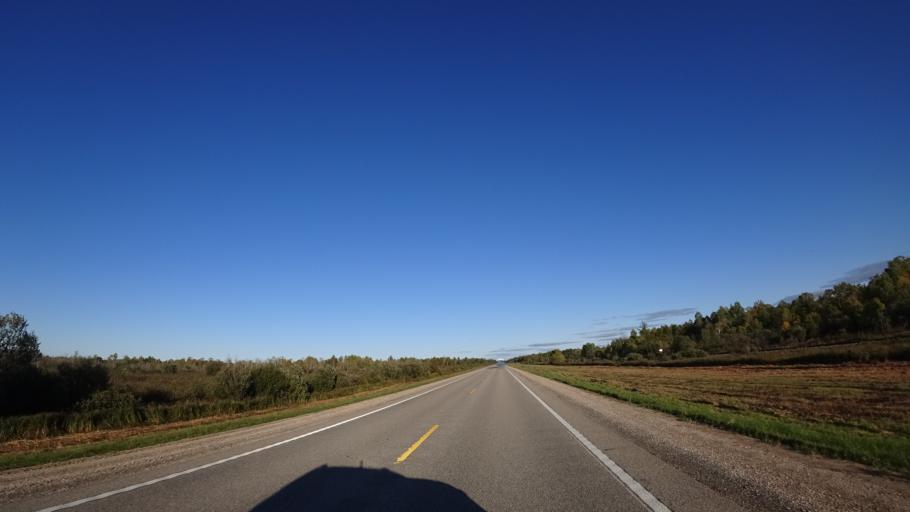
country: US
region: Michigan
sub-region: Schoolcraft County
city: Manistique
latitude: 46.3455
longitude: -86.1437
